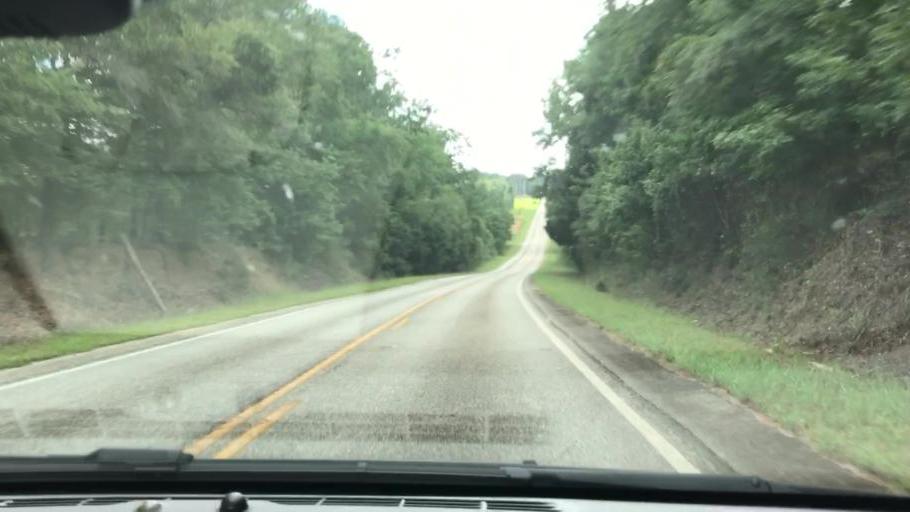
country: US
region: Georgia
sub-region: Stewart County
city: Lumpkin
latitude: 32.0579
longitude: -84.8141
